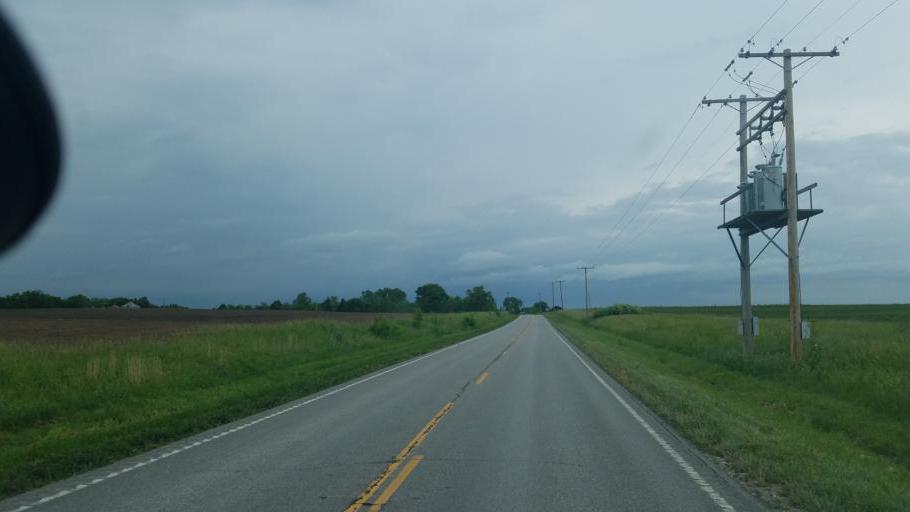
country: US
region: Missouri
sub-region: Cooper County
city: Boonville
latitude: 38.8840
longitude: -92.6516
